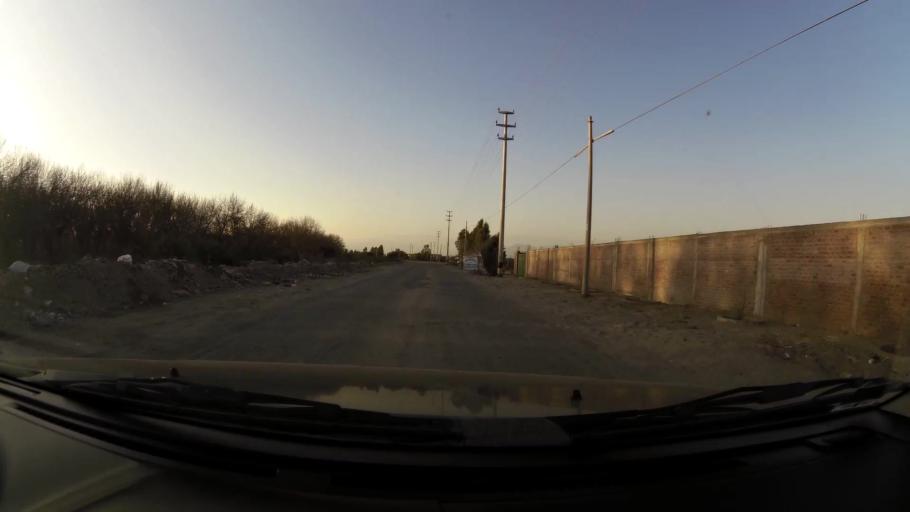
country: PE
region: Ica
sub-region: Provincia de Ica
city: Ica
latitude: -14.0873
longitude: -75.7179
